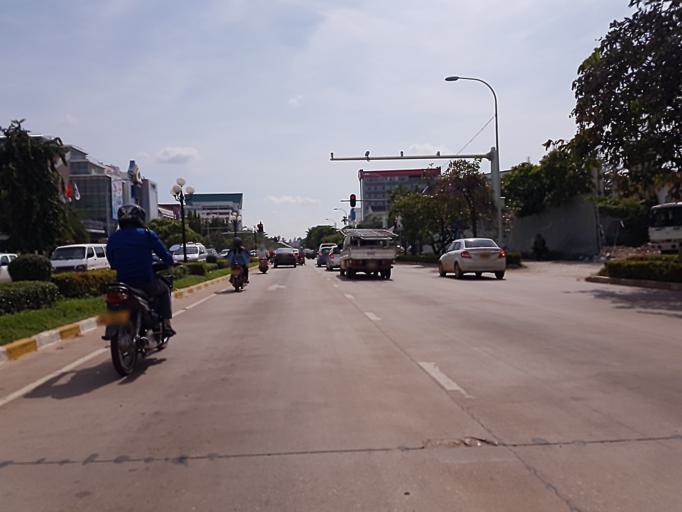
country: LA
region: Vientiane
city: Vientiane
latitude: 17.9683
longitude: 102.6164
